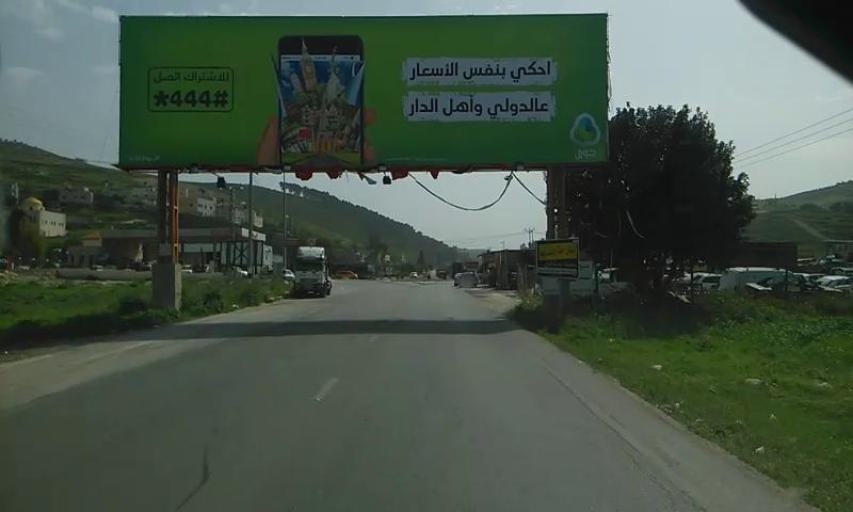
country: PS
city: Bir al Basha
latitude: 32.4088
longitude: 35.2273
